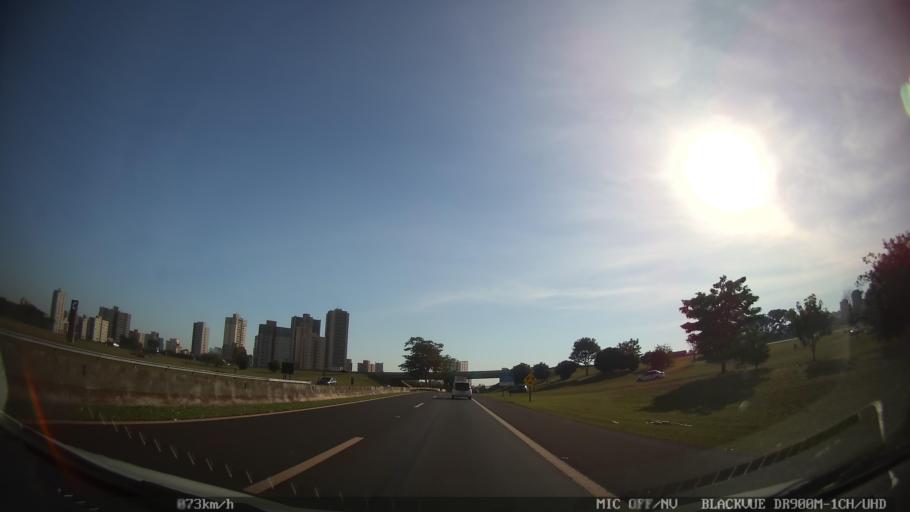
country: BR
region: Sao Paulo
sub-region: Ribeirao Preto
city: Ribeirao Preto
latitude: -21.2247
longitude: -47.8171
